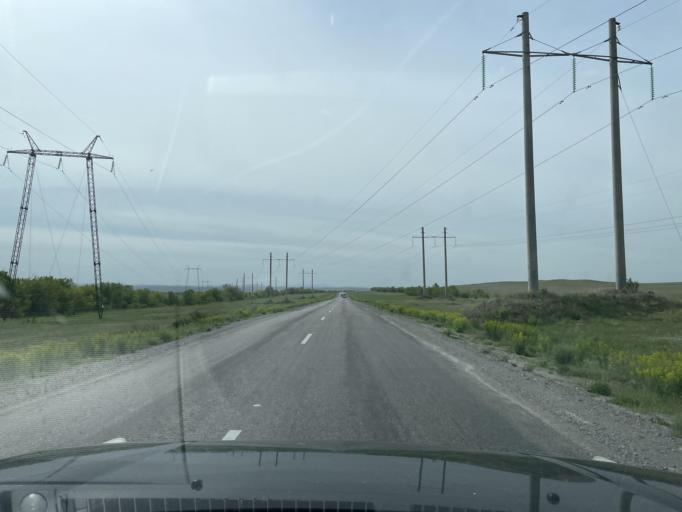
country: KZ
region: Qaraghandy
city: Abay
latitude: 49.4673
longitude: 72.9207
